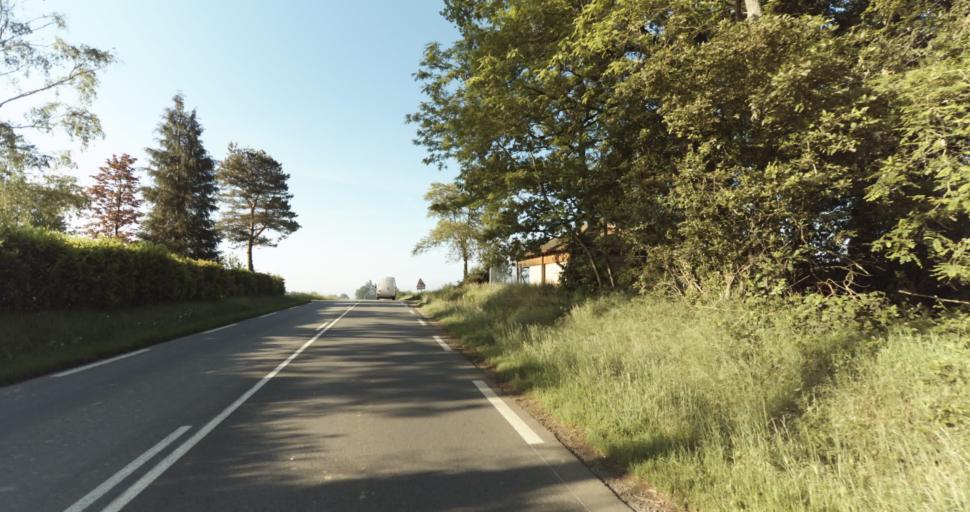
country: FR
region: Limousin
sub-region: Departement de la Haute-Vienne
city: Condat-sur-Vienne
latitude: 45.7784
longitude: 1.2889
